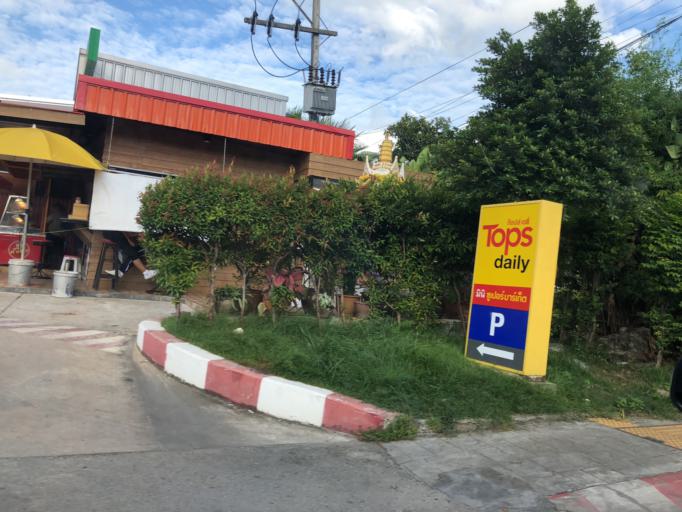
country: TH
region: Phuket
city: Wichit
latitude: 7.8902
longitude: 98.3901
